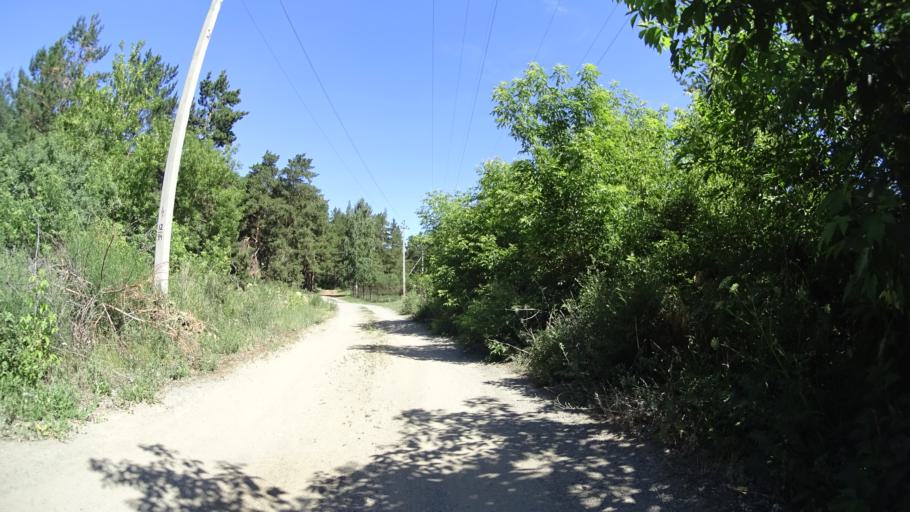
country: RU
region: Chelyabinsk
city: Troitsk
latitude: 54.0520
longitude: 61.6269
